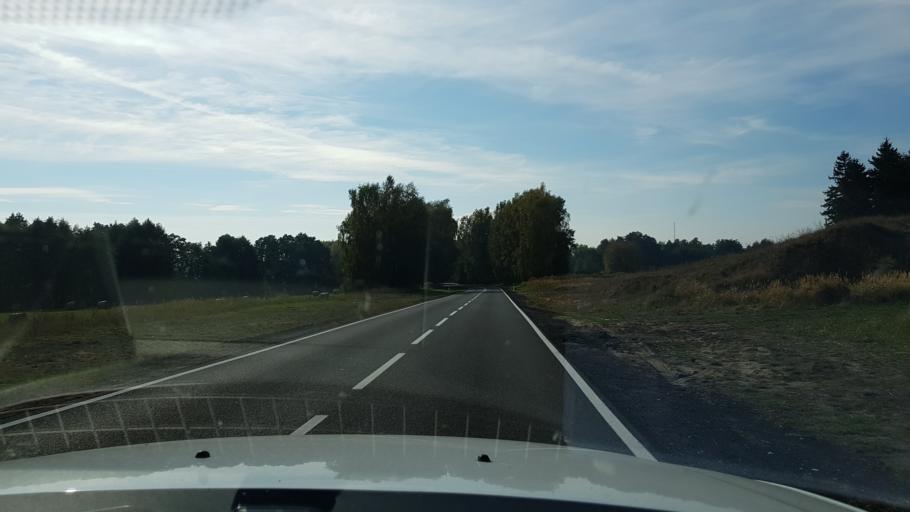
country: PL
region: West Pomeranian Voivodeship
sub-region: Powiat gryfinski
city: Chojna
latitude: 52.9614
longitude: 14.4626
